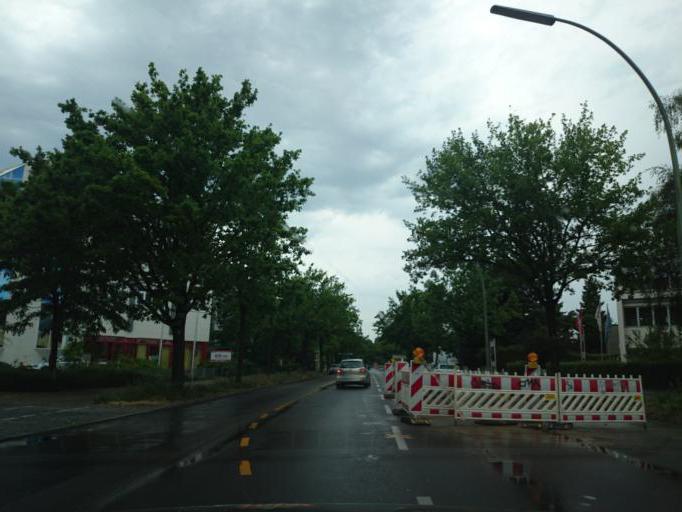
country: DE
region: Berlin
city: Marienfelde
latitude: 52.4067
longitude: 13.3792
